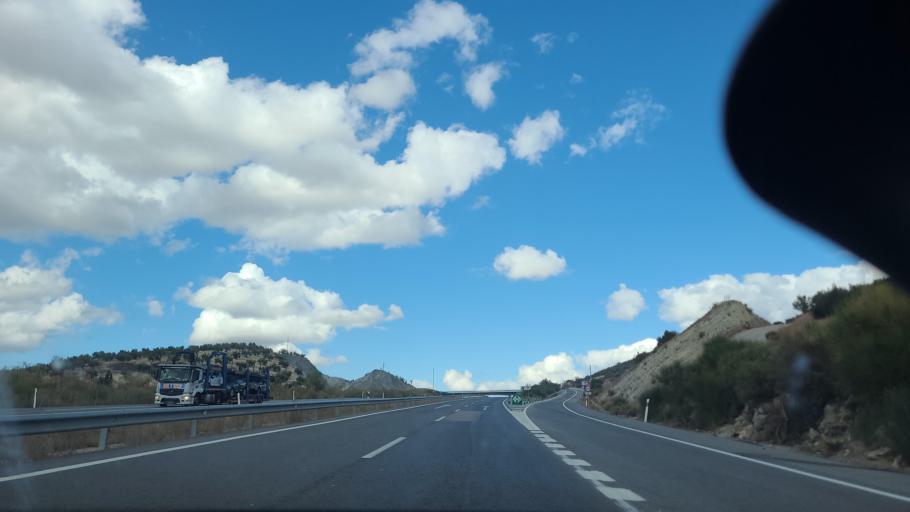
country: ES
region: Andalusia
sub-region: Provincia de Jaen
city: Noalejo
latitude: 37.5283
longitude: -3.6366
